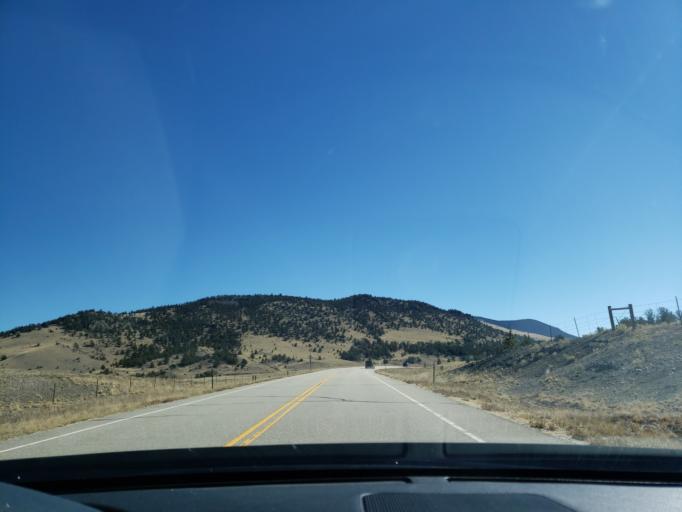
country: US
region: Colorado
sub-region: Chaffee County
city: Buena Vista
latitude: 38.8629
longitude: -105.6611
